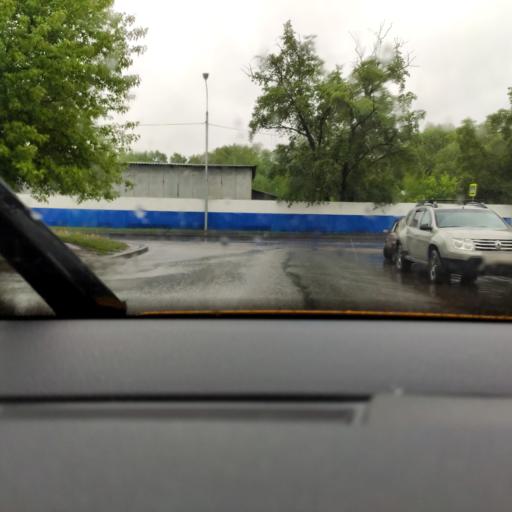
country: RU
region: Moscow
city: Strogino
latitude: 55.8384
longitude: 37.4246
